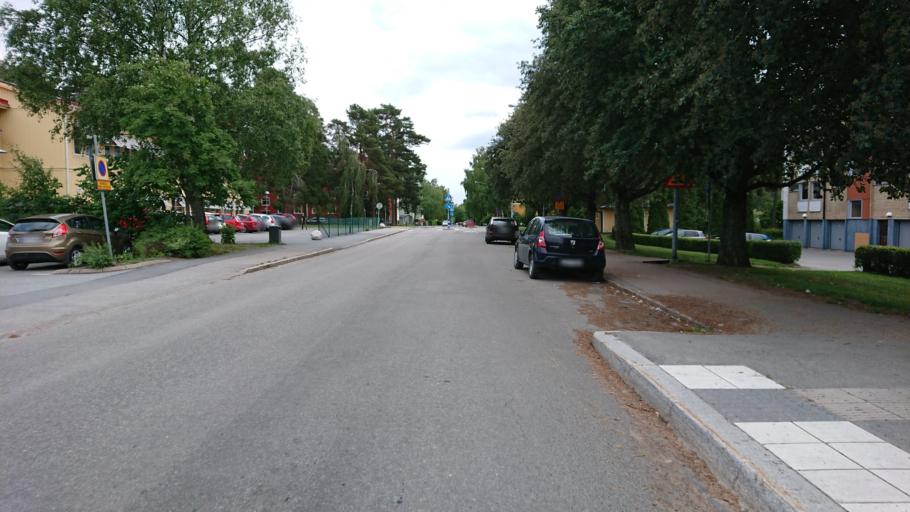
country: SE
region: Uppsala
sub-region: Uppsala Kommun
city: Gamla Uppsala
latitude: 59.8776
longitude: 17.6197
